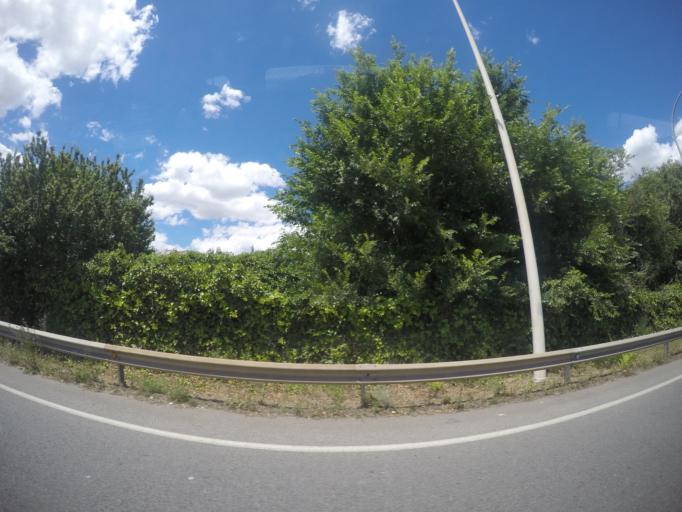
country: ES
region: Catalonia
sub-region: Provincia de Barcelona
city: Badalona
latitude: 41.4558
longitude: 2.2466
